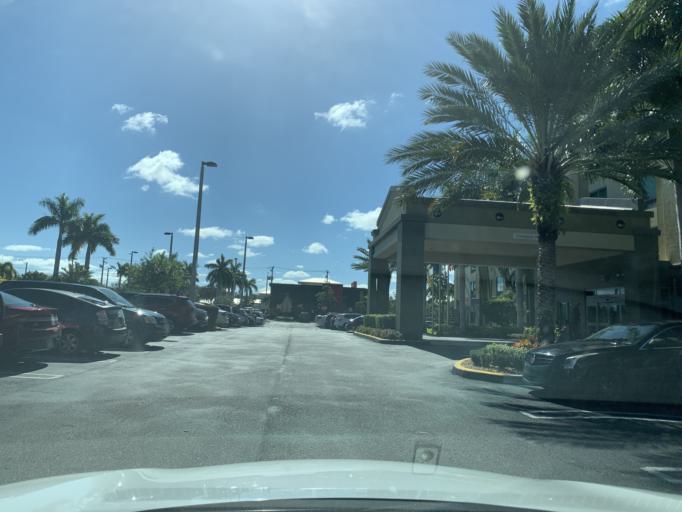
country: US
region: Florida
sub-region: Broward County
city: Dania Beach
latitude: 26.0641
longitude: -80.1677
